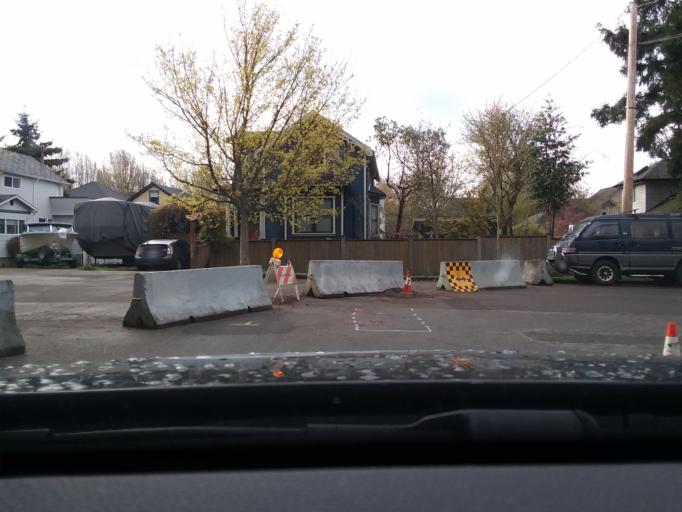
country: CA
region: British Columbia
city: Victoria
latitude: 48.4372
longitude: -123.3918
